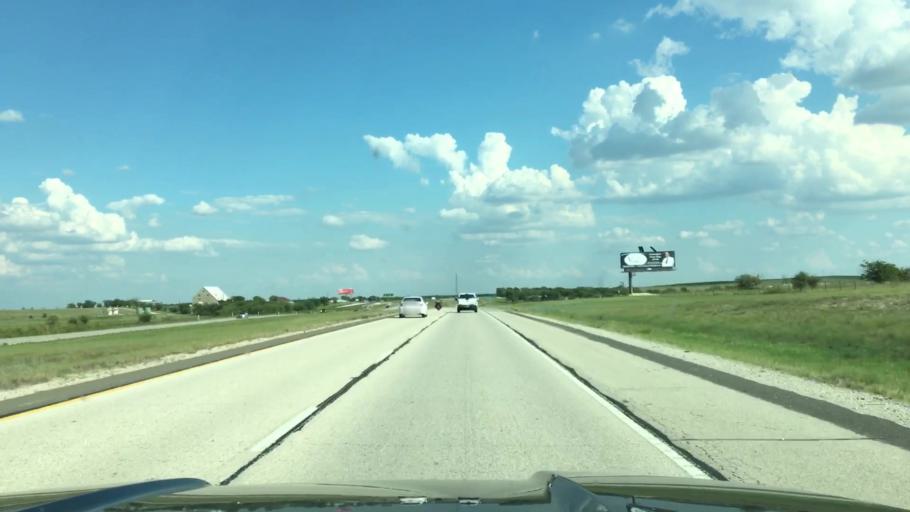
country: US
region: Texas
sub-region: Wise County
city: New Fairview
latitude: 33.1544
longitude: -97.5162
